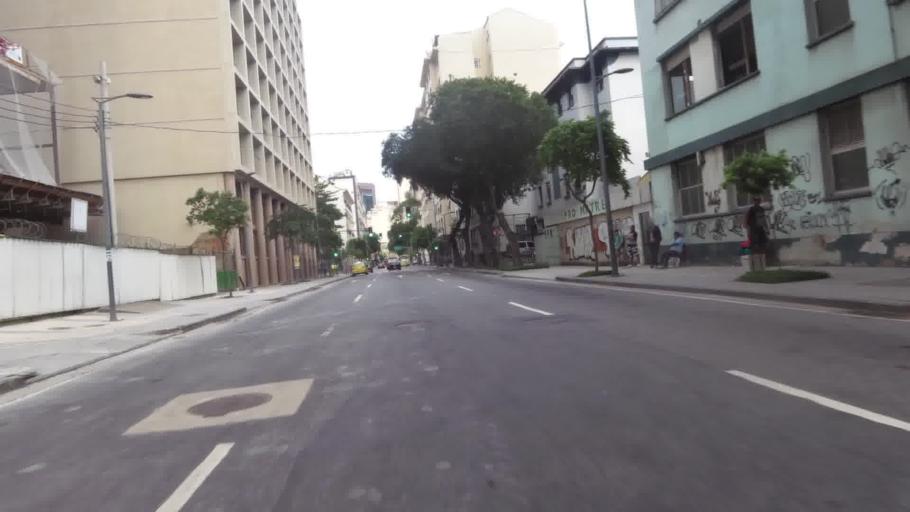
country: BR
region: Rio de Janeiro
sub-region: Rio De Janeiro
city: Rio de Janeiro
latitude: -22.8958
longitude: -43.1865
